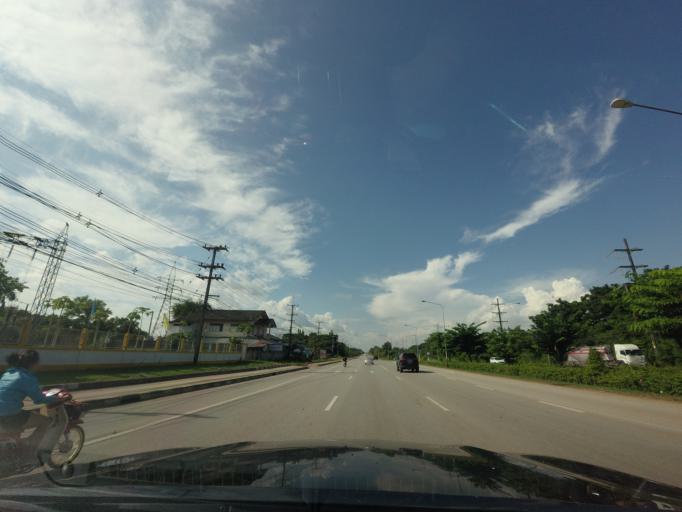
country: TH
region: Nong Khai
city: Nong Khai
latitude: 17.8218
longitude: 102.7571
